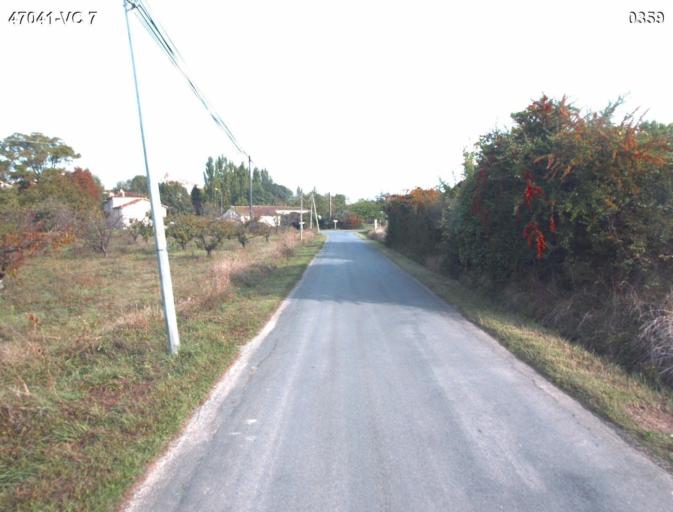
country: FR
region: Aquitaine
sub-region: Departement du Lot-et-Garonne
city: Port-Sainte-Marie
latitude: 44.2026
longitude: 0.4136
